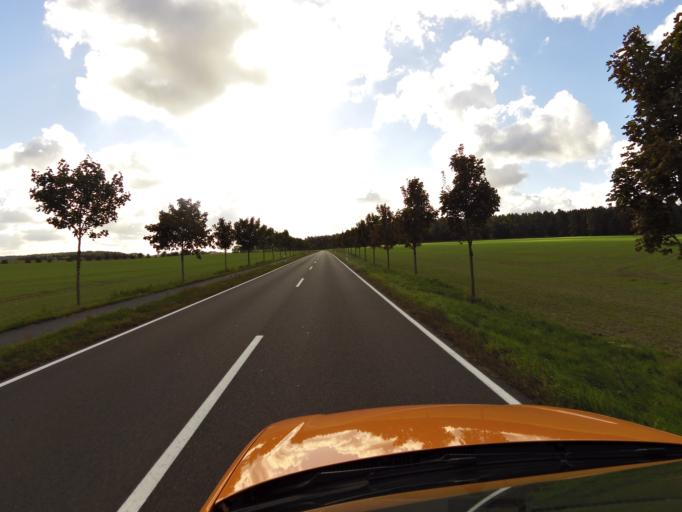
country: DE
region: Brandenburg
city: Michendorf
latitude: 52.2786
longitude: 13.0700
